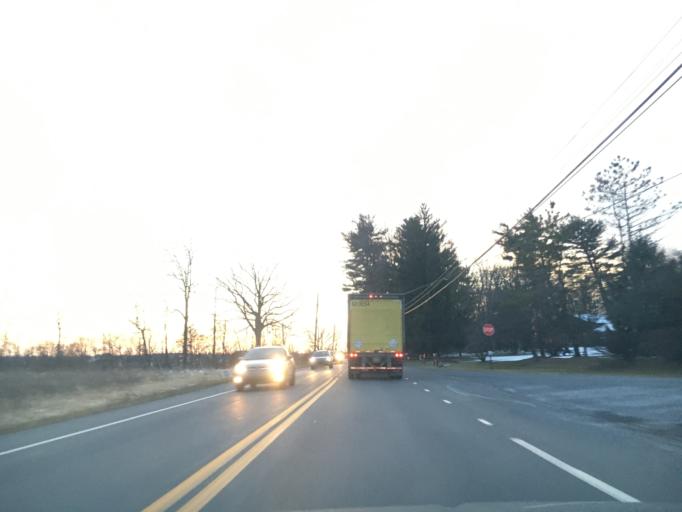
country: US
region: Pennsylvania
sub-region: Northampton County
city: Nazareth
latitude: 40.7959
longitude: -75.3560
